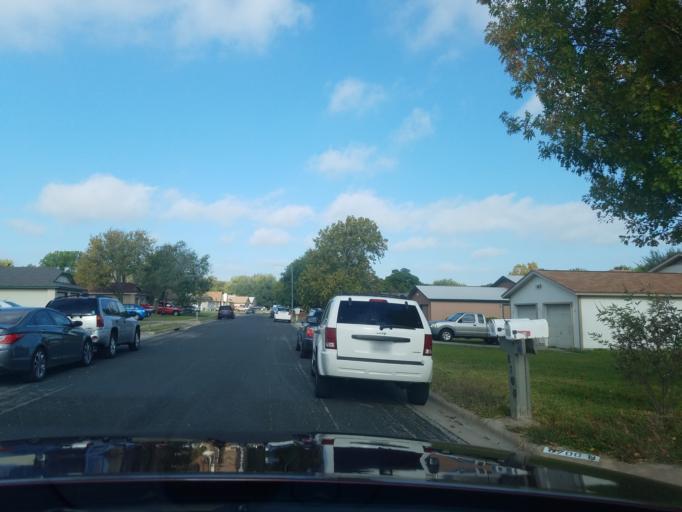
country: US
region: Texas
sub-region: Williamson County
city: Jollyville
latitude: 30.4485
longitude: -97.7748
